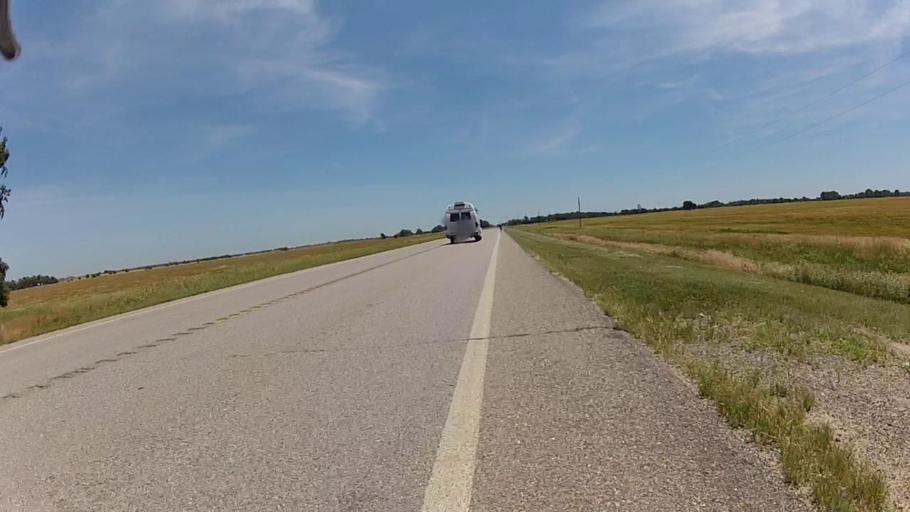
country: US
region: Kansas
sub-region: Barber County
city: Medicine Lodge
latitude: 37.2534
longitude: -98.4452
